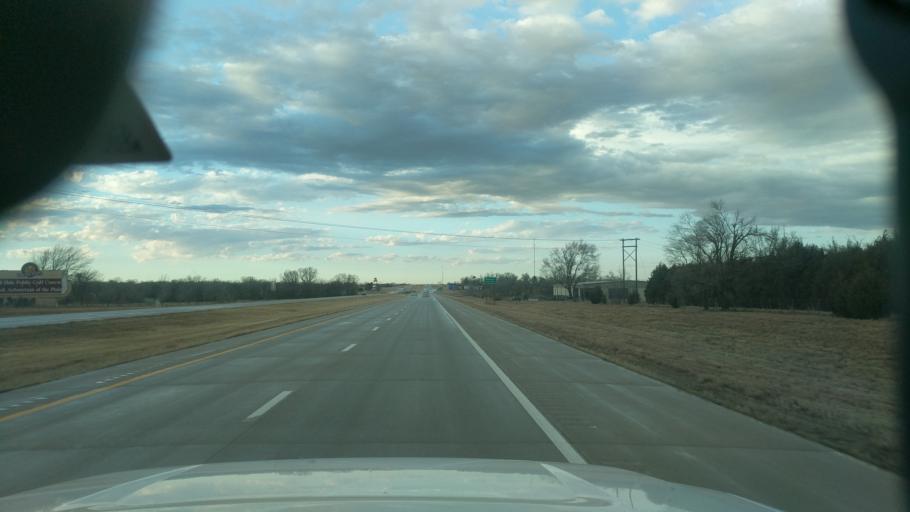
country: US
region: Kansas
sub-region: Harvey County
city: Hesston
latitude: 38.1372
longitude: -97.4080
